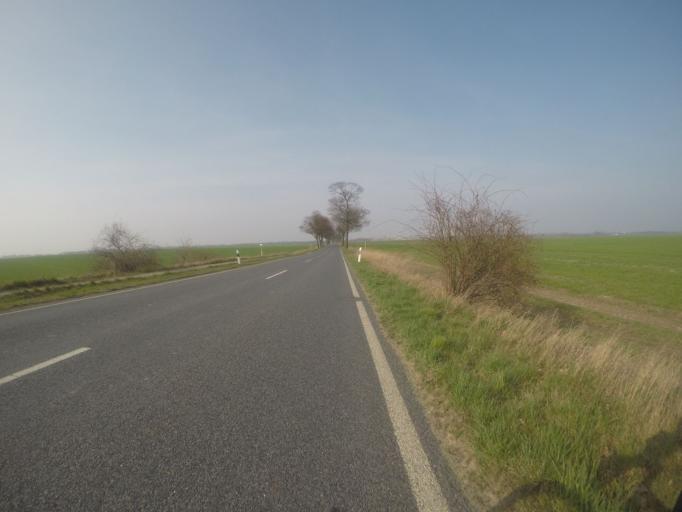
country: DE
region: Brandenburg
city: Schonefeld
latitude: 52.3212
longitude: 13.5072
